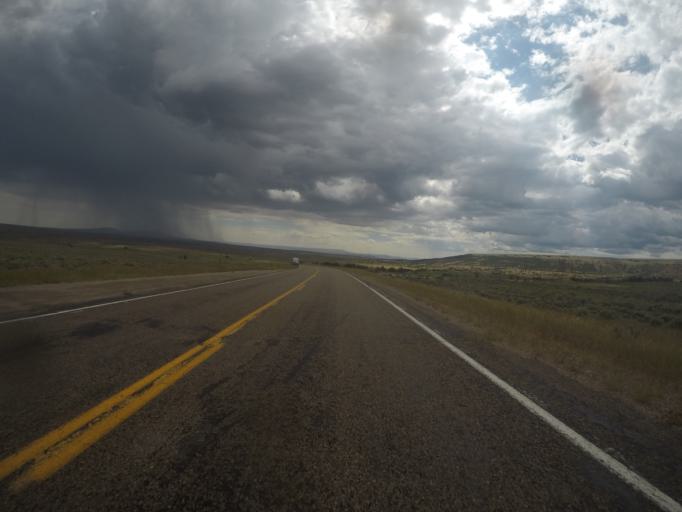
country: US
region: Utah
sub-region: Daggett County
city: Manila
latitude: 41.0219
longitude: -109.8970
